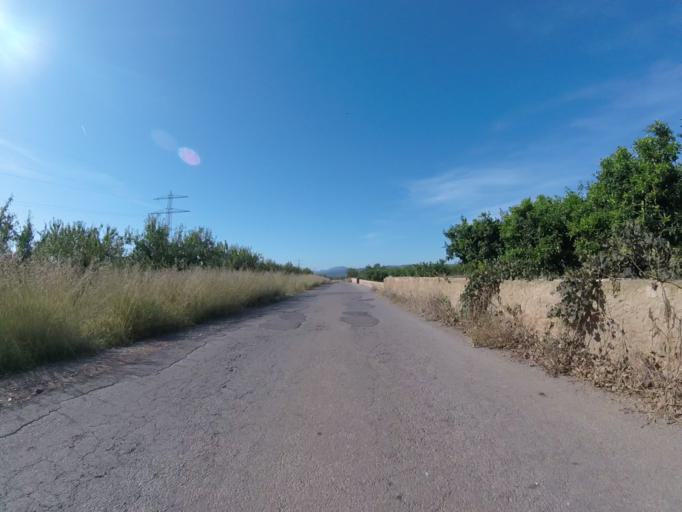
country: ES
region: Valencia
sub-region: Provincia de Castello
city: Torreblanca
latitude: 40.2134
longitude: 0.2141
